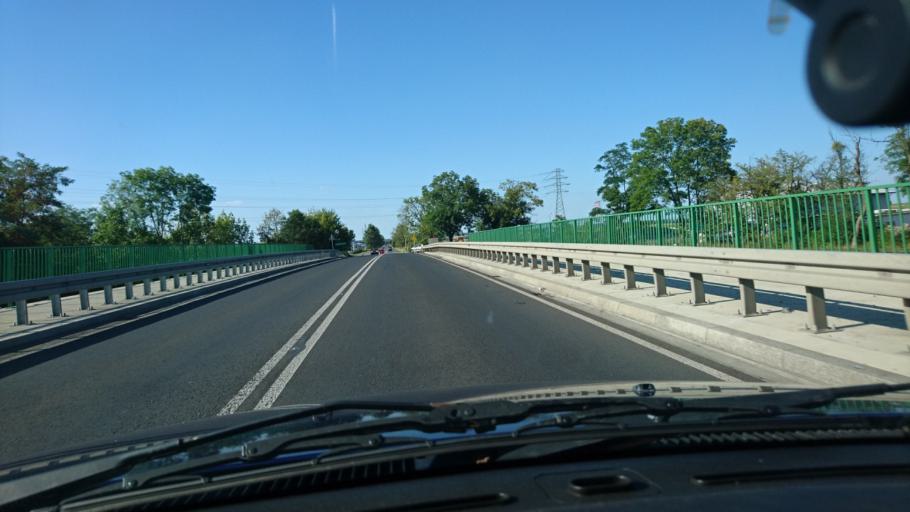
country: PL
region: Silesian Voivodeship
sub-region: Powiat gliwicki
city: Pyskowice
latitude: 50.3734
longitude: 18.6349
